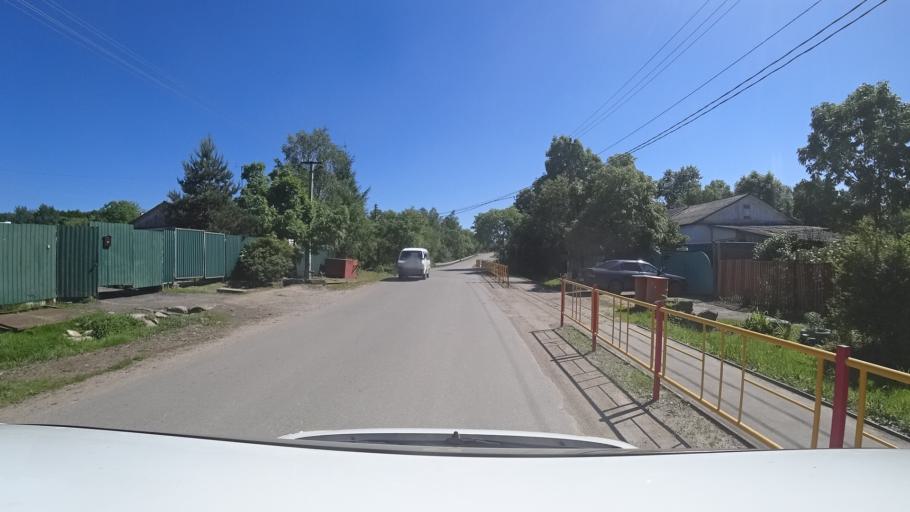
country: RU
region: Khabarovsk Krai
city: Topolevo
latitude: 48.5600
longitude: 135.1927
